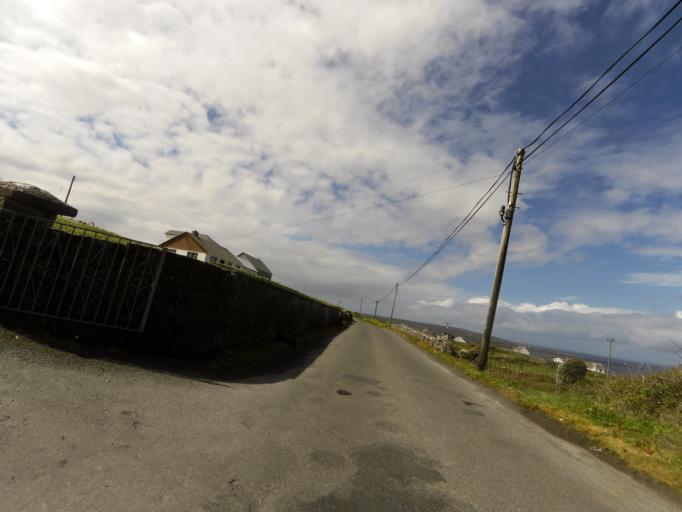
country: IE
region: Connaught
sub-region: County Galway
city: Clifden
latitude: 53.1308
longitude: -9.7208
